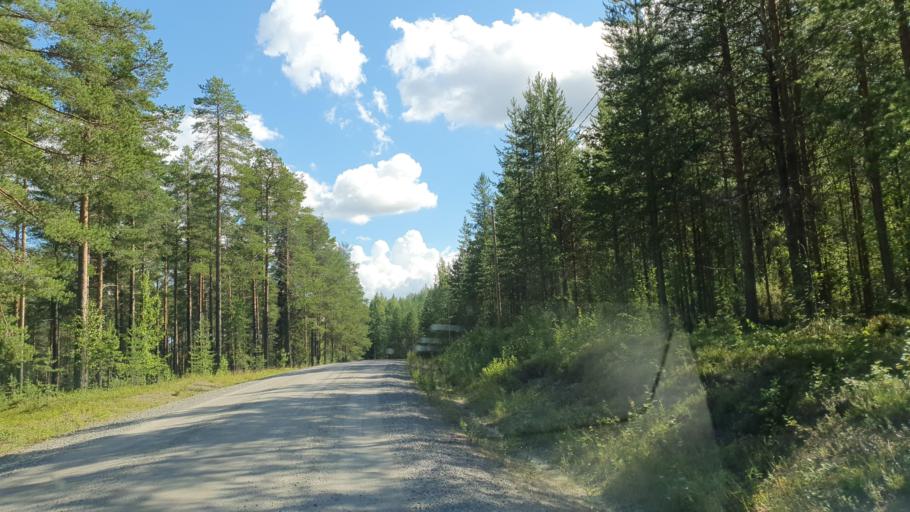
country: FI
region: Kainuu
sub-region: Kehys-Kainuu
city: Kuhmo
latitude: 64.1044
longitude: 29.3993
